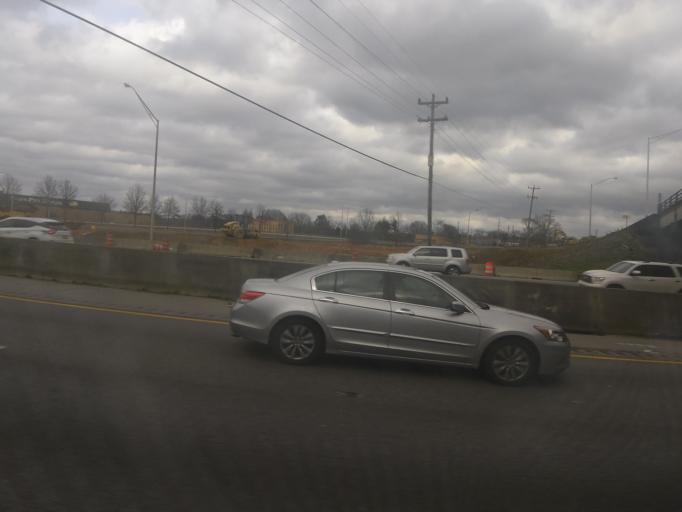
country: US
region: Georgia
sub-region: Catoosa County
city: Indian Springs
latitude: 34.9902
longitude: -85.2041
